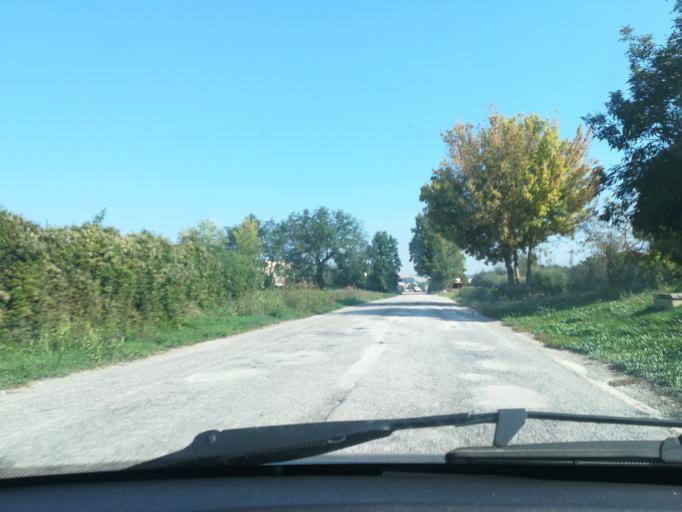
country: IT
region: The Marches
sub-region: Provincia di Macerata
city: Piediripa
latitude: 43.2721
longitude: 13.4707
